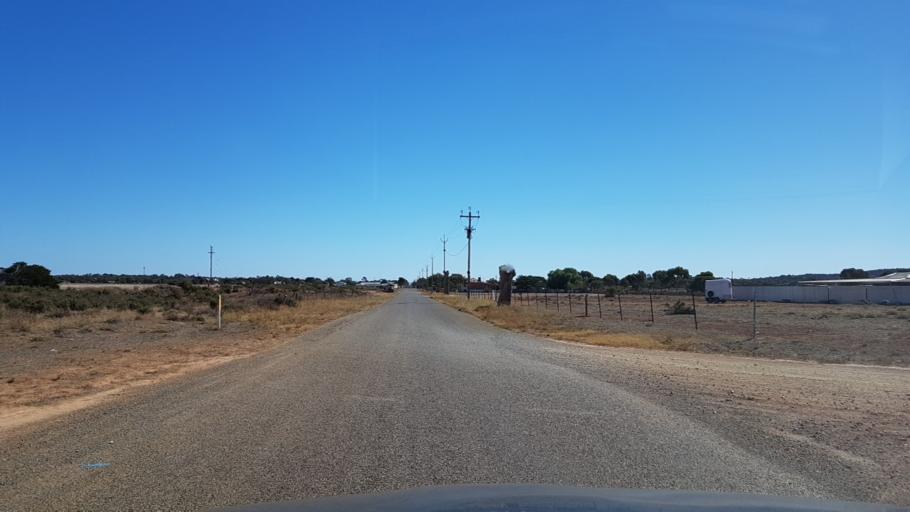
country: AU
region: South Australia
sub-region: Peterborough
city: Peterborough
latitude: -32.9717
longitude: 138.8547
